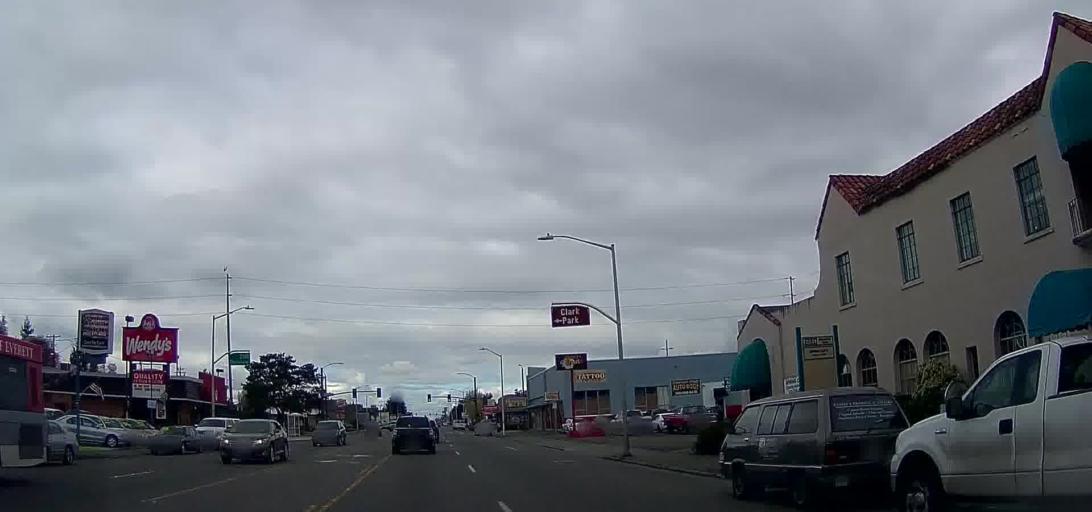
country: US
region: Washington
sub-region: Snohomish County
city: Everett
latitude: 47.9833
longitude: -122.2015
